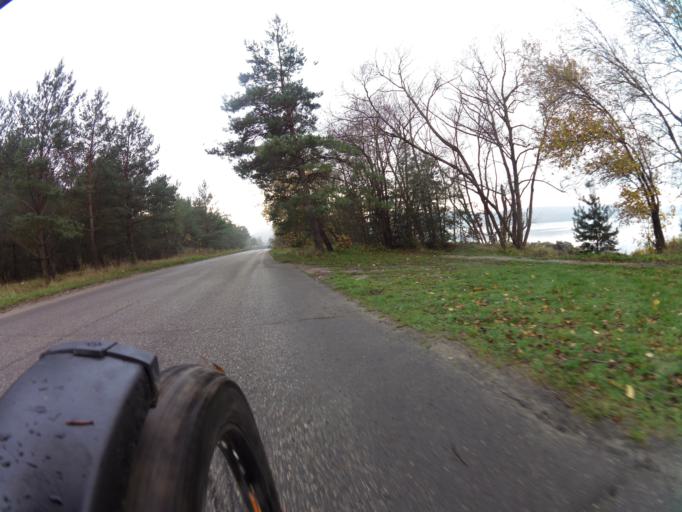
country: PL
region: Pomeranian Voivodeship
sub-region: Powiat wejherowski
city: Gniewino
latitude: 54.7343
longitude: 18.0920
